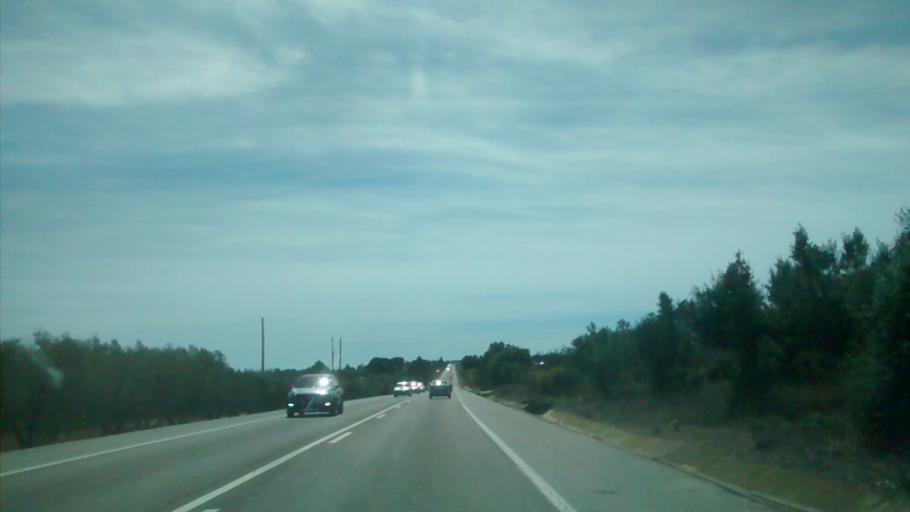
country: ES
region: Catalonia
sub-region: Provincia de Tarragona
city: Sant Carles de la Rapita
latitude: 40.6570
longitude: 0.5885
